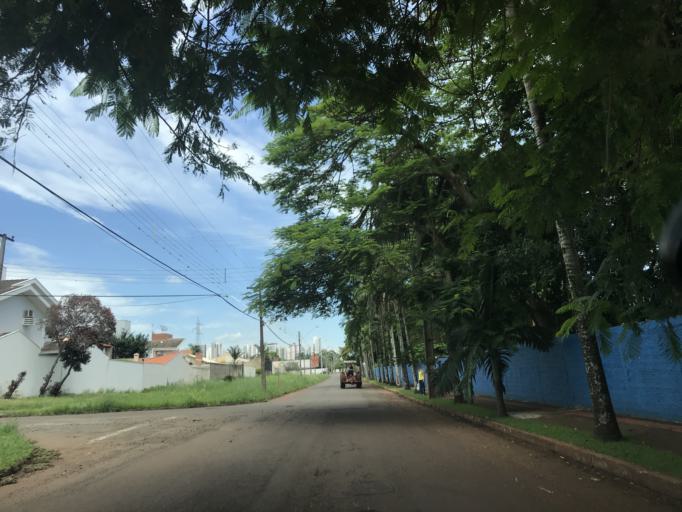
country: BR
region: Parana
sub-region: Londrina
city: Londrina
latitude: -23.3431
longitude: -51.1560
